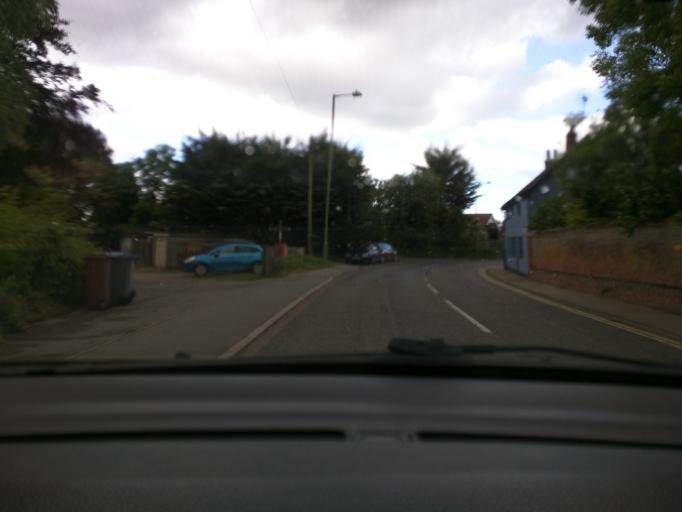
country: GB
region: England
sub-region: Suffolk
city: Framlingham
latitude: 52.2219
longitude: 1.3481
